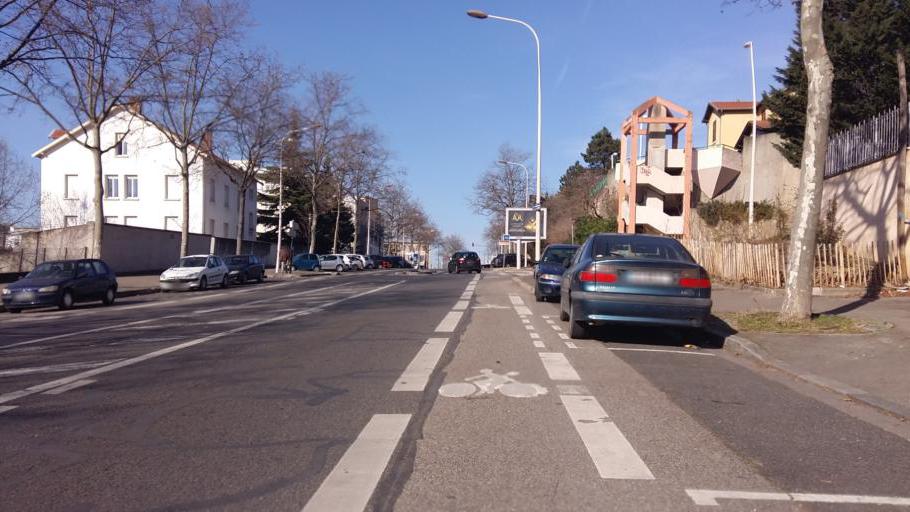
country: FR
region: Rhone-Alpes
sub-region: Departement du Rhone
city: Villeurbanne
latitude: 45.7393
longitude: 4.8850
